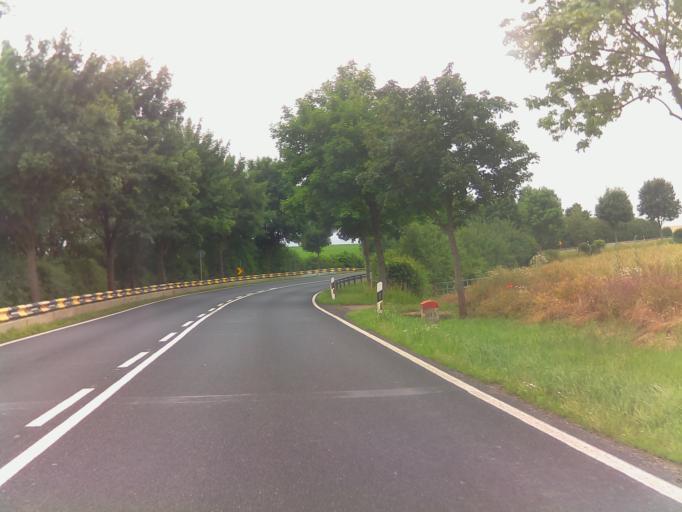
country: LU
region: Luxembourg
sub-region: Canton de Capellen
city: Garnich
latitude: 49.6295
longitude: 5.9564
